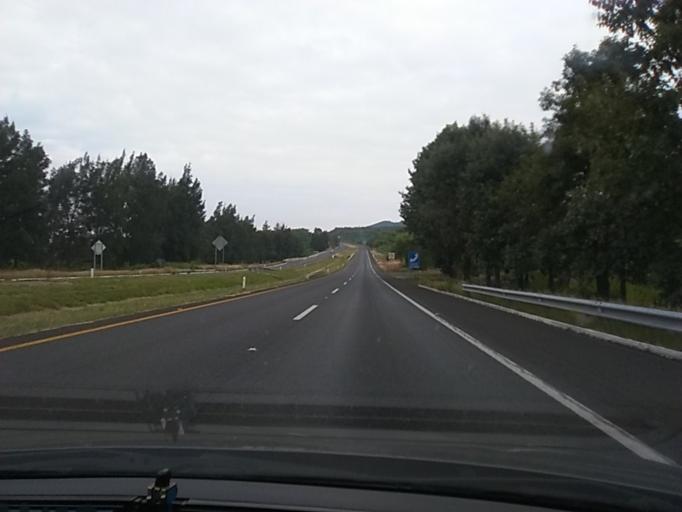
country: MX
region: Michoacan
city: Panindicuaro de la Reforma
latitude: 19.9711
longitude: -101.7204
